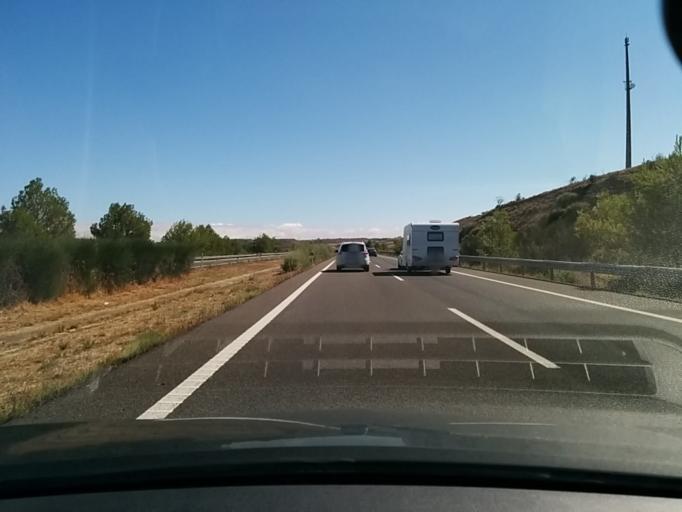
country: ES
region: Aragon
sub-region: Provincia de Huesca
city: Almudebar
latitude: 42.0469
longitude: -0.5596
